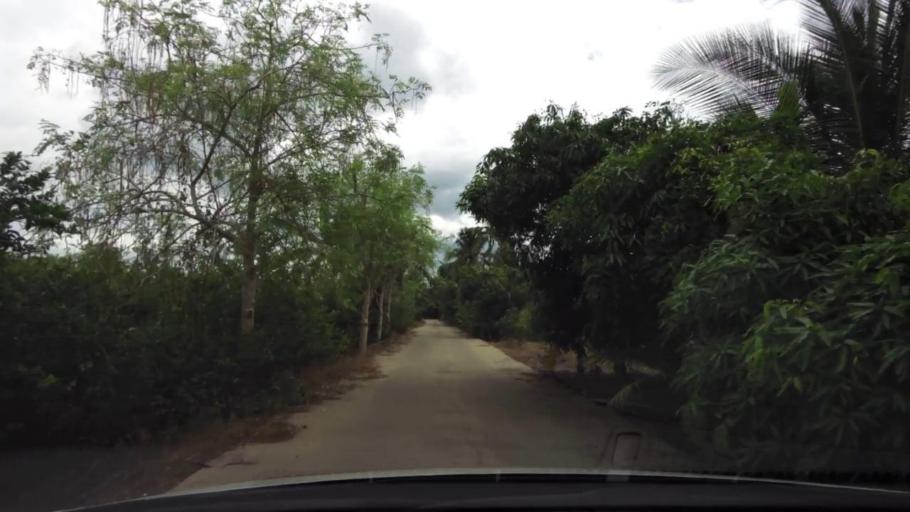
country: TH
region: Ratchaburi
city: Damnoen Saduak
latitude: 13.5562
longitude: 99.9917
